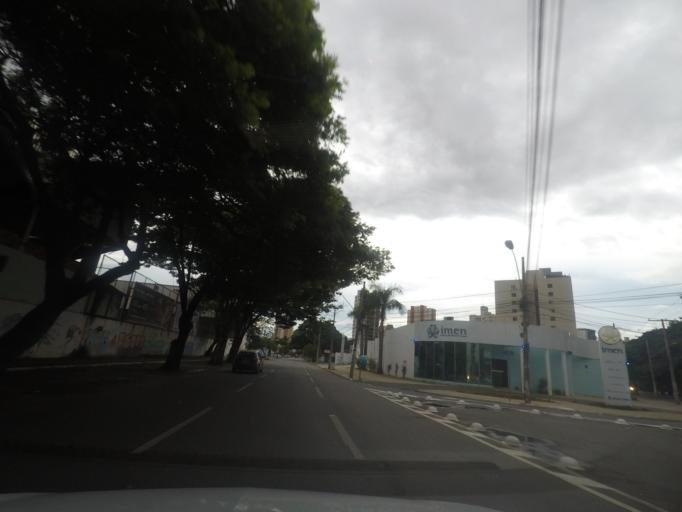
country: BR
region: Goias
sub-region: Goiania
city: Goiania
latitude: -16.6779
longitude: -49.2641
